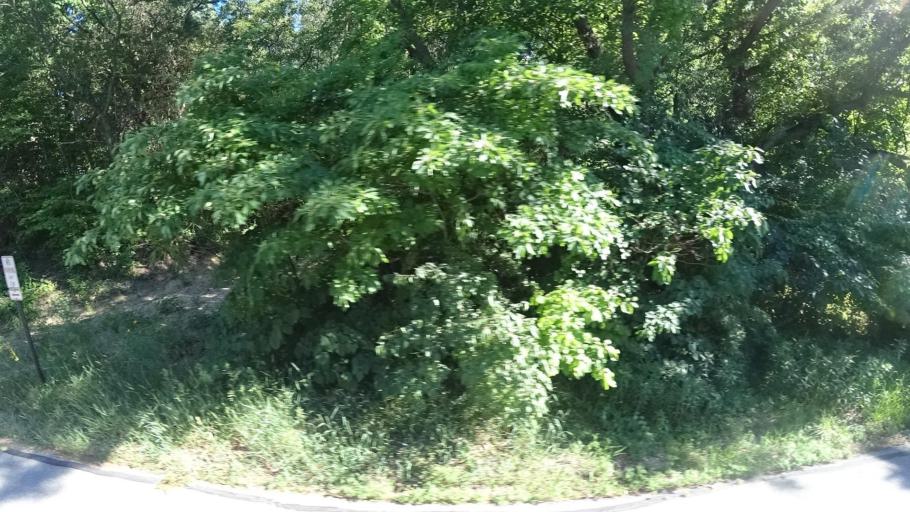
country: US
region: Indiana
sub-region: Porter County
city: Porter
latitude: 41.6569
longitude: -87.0703
